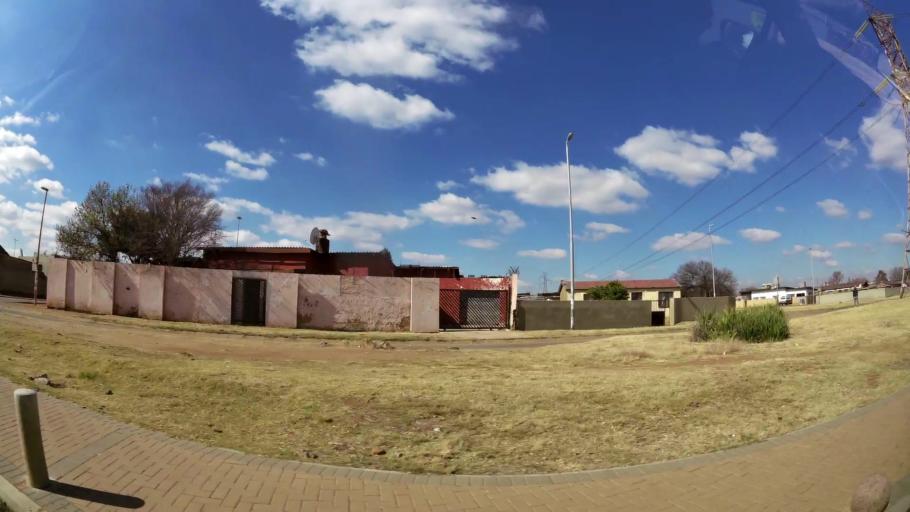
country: ZA
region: Gauteng
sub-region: West Rand District Municipality
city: Krugersdorp
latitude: -26.1405
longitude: 27.7937
